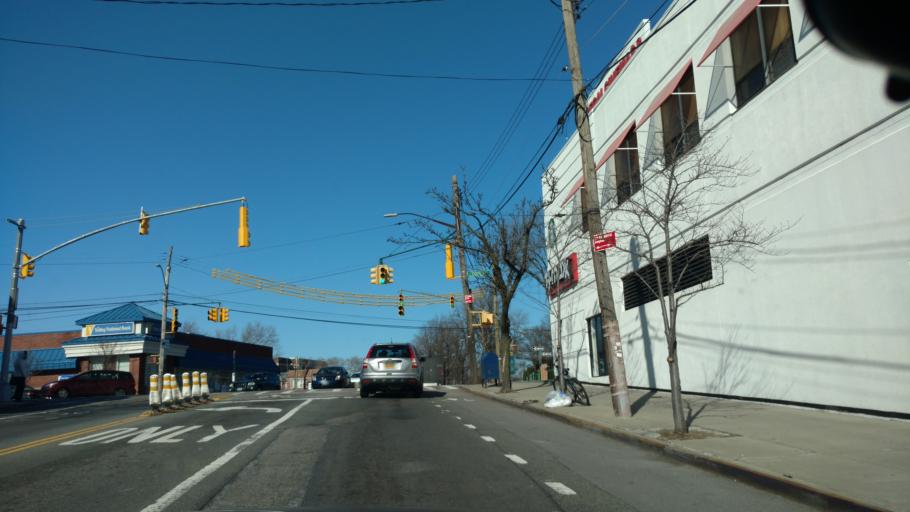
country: US
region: New York
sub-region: Queens County
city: Borough of Queens
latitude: 40.7089
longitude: -73.8699
